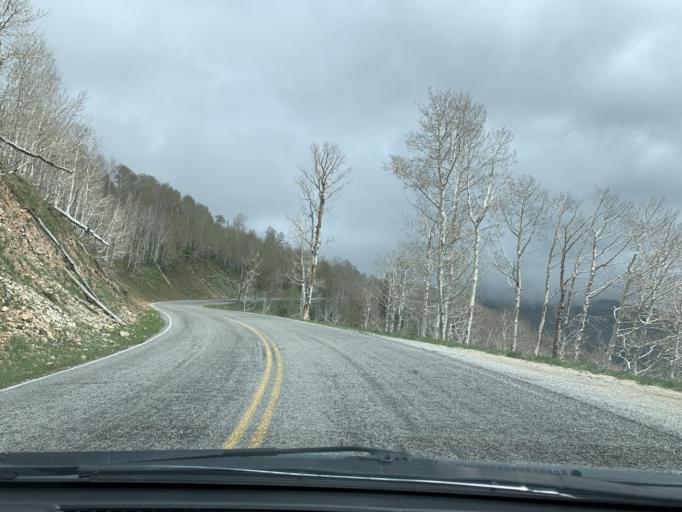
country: US
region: Utah
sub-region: Utah County
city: Elk Ridge
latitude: 39.8737
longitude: -111.6841
